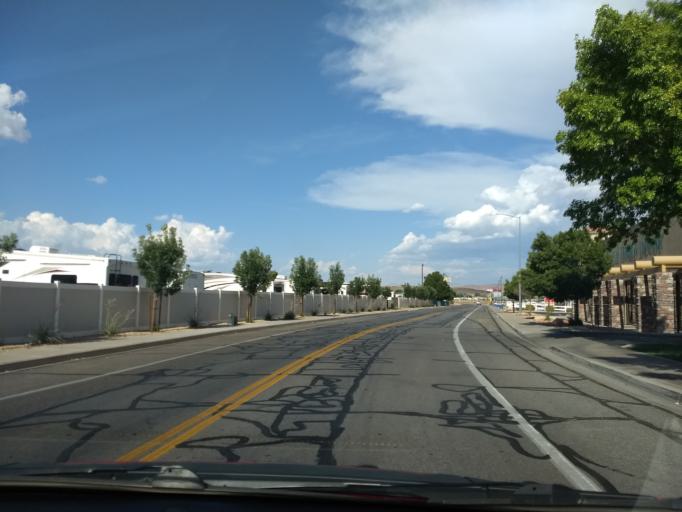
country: US
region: Utah
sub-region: Washington County
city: Saint George
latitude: 37.0885
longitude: -113.5822
